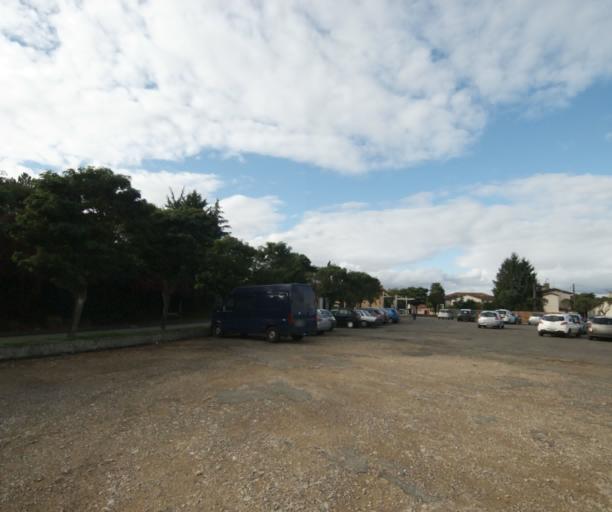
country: FR
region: Midi-Pyrenees
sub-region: Departement du Gers
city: Eauze
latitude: 43.8586
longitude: 0.1031
